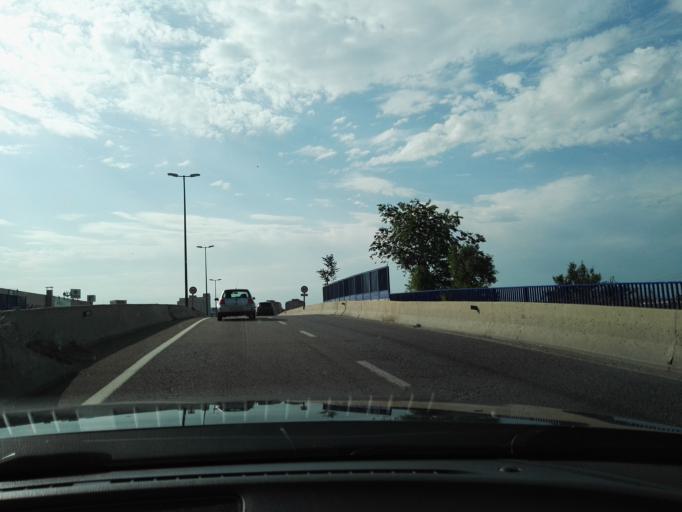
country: ES
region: Aragon
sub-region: Provincia de Zaragoza
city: Zaragoza
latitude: 41.6302
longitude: -0.8561
